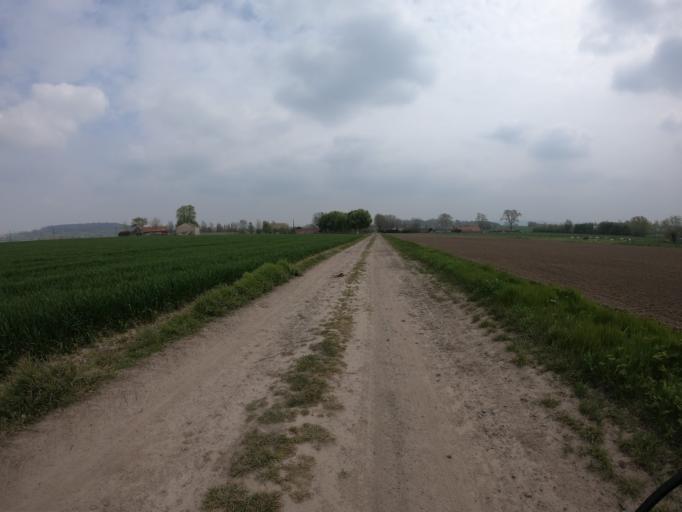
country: BE
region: Flanders
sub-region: Provincie Oost-Vlaanderen
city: Ronse
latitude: 50.7414
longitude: 3.5498
